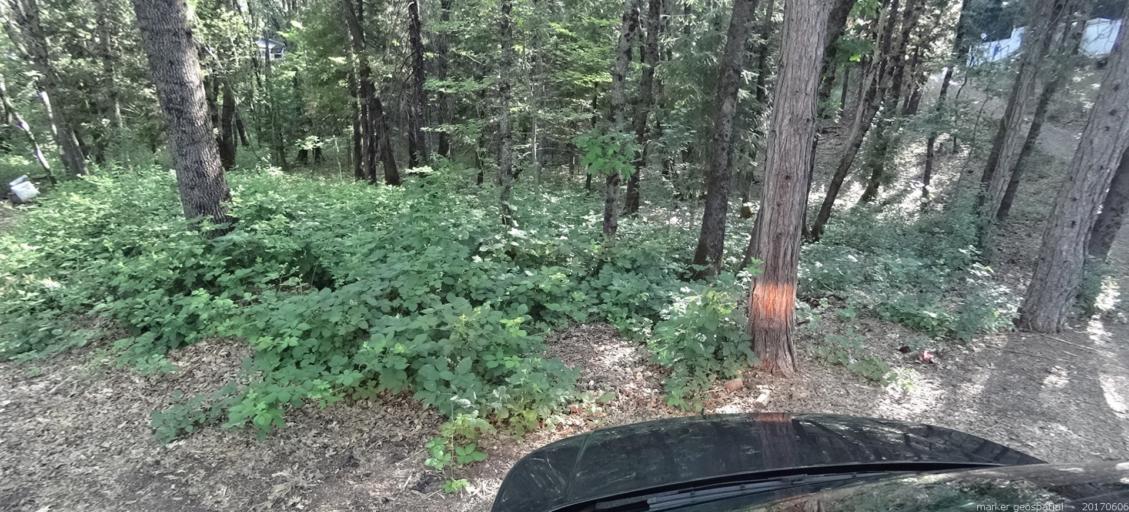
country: US
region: California
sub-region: Siskiyou County
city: Dunsmuir
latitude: 41.2021
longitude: -122.2691
